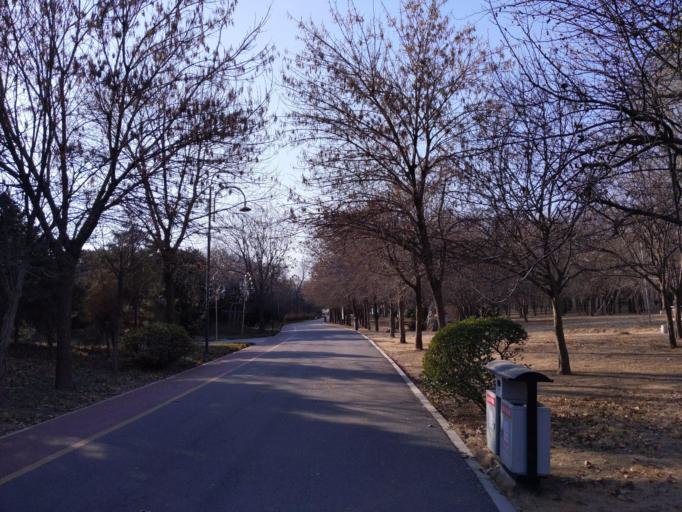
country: CN
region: Henan Sheng
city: Puyang
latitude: 35.7789
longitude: 114.9628
